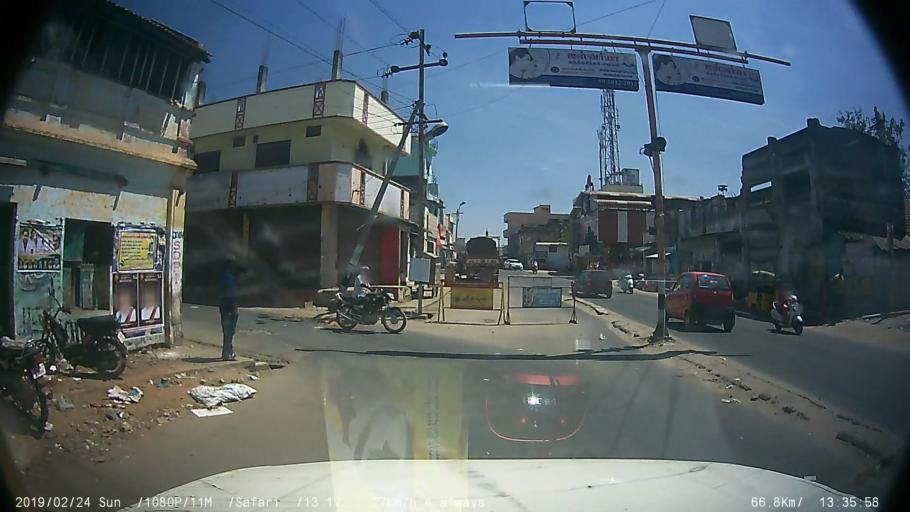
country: IN
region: Tamil Nadu
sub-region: Coimbatore
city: Mettupalayam
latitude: 11.3101
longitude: 76.9317
